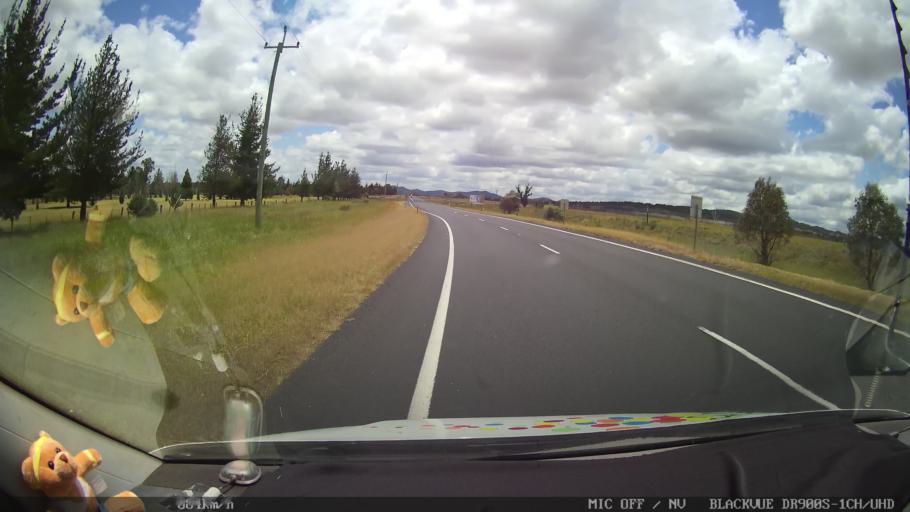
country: AU
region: New South Wales
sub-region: Glen Innes Severn
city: Glen Innes
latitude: -29.4335
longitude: 151.8533
